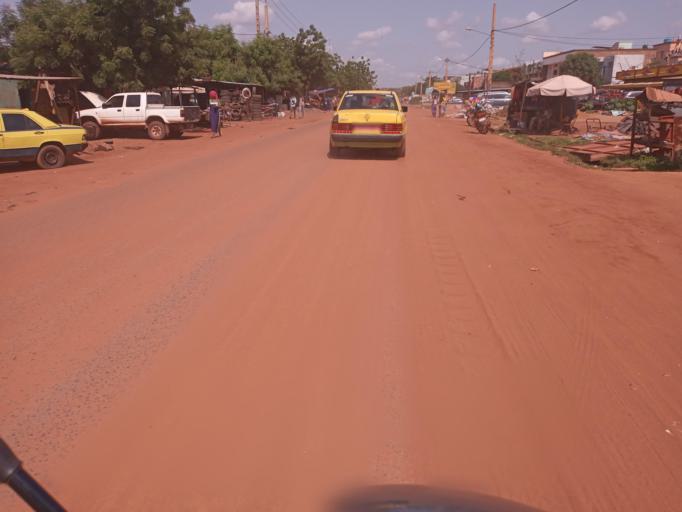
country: ML
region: Bamako
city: Bamako
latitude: 12.5968
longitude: -8.0204
